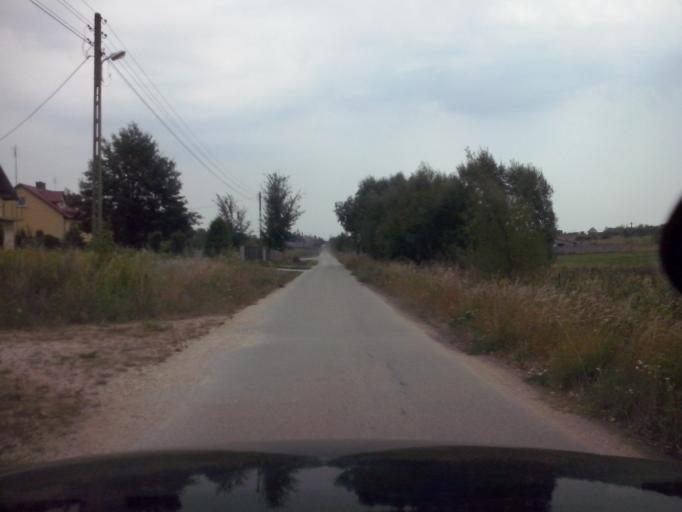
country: PL
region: Swietokrzyskie
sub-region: Powiat kielecki
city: Brzeziny
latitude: 50.7824
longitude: 20.5513
